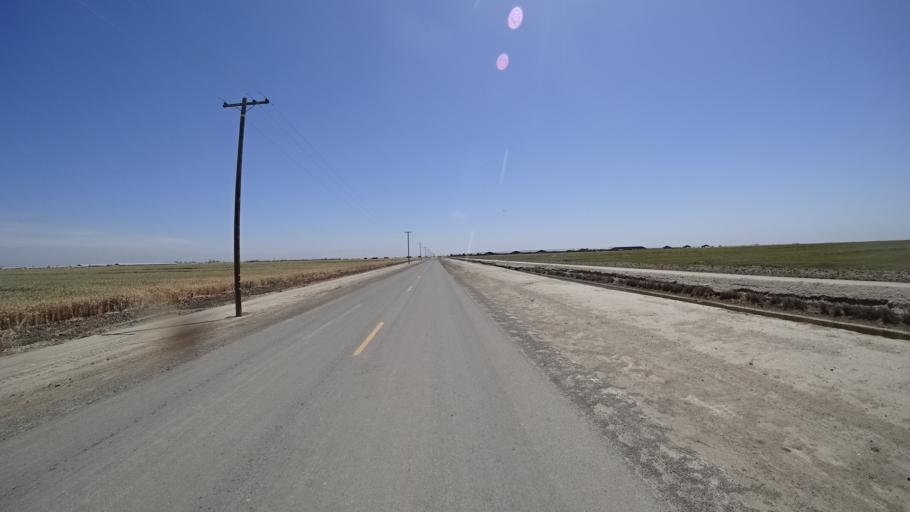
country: US
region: California
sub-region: Kings County
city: Stratford
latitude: 36.1893
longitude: -119.6993
